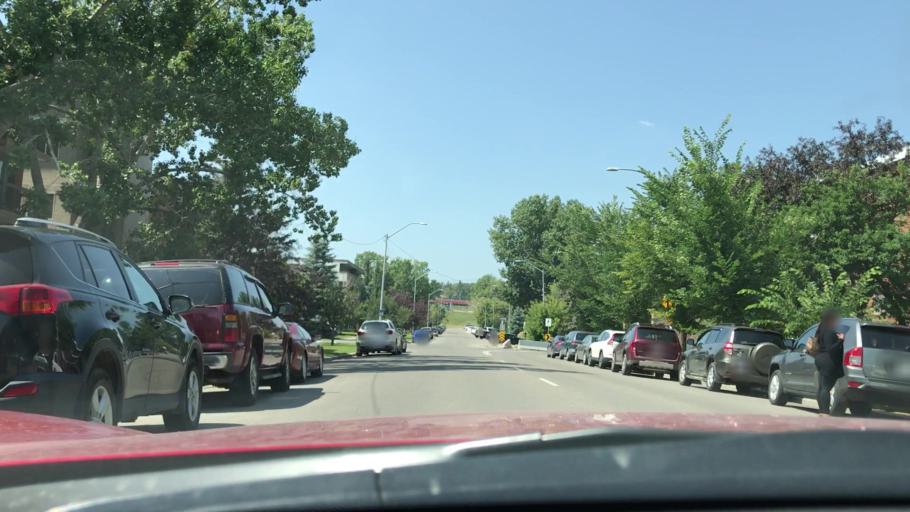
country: CA
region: Alberta
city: Calgary
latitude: 51.0435
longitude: -114.1031
